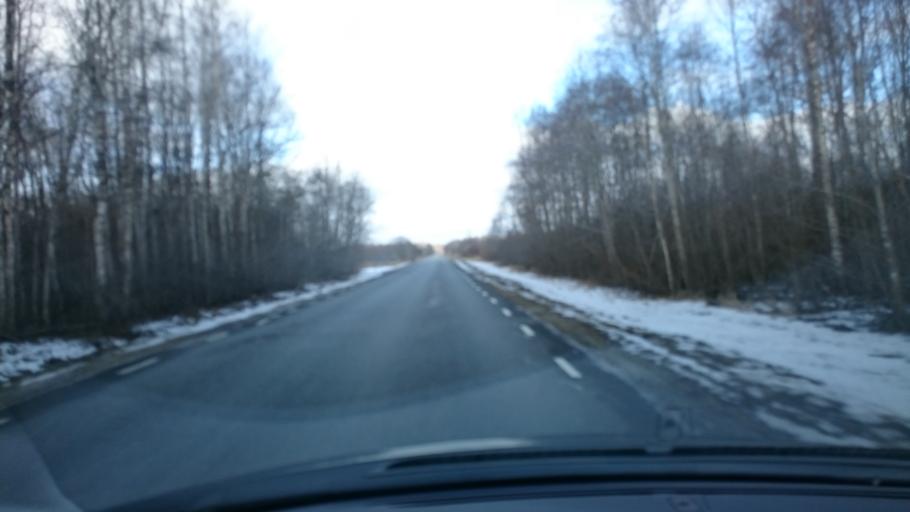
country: EE
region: Harju
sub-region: Keila linn
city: Keila
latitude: 59.3728
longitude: 24.3139
